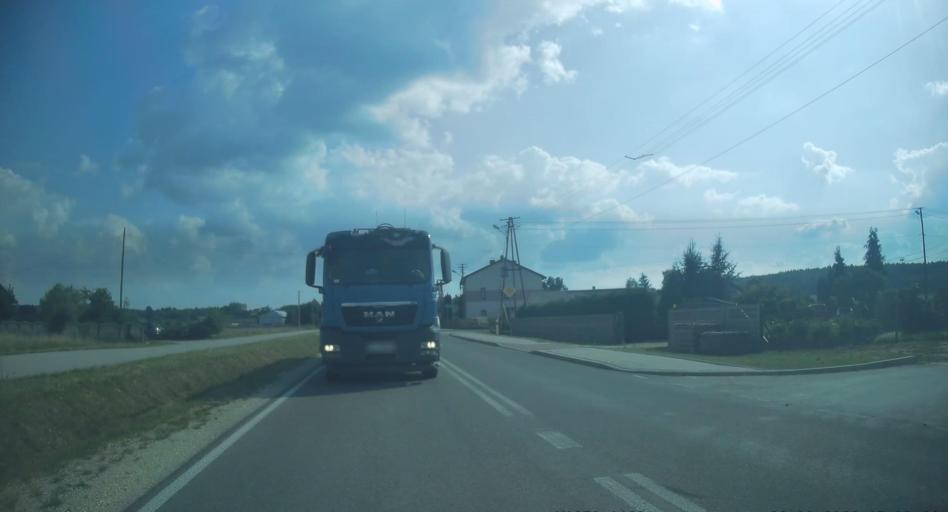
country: PL
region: Swietokrzyskie
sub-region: Powiat konecki
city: Radoszyce
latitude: 51.0443
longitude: 20.2834
